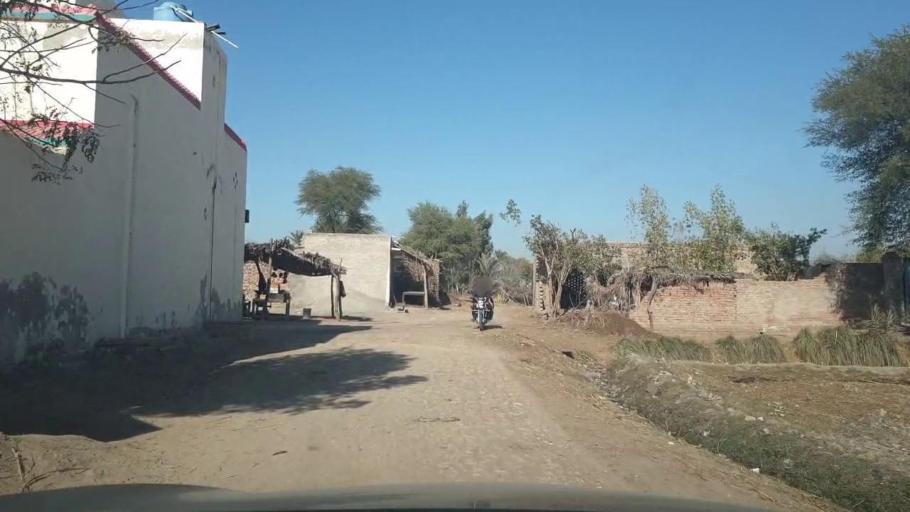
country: PK
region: Sindh
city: Mirpur Mathelo
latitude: 28.0813
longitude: 69.4893
